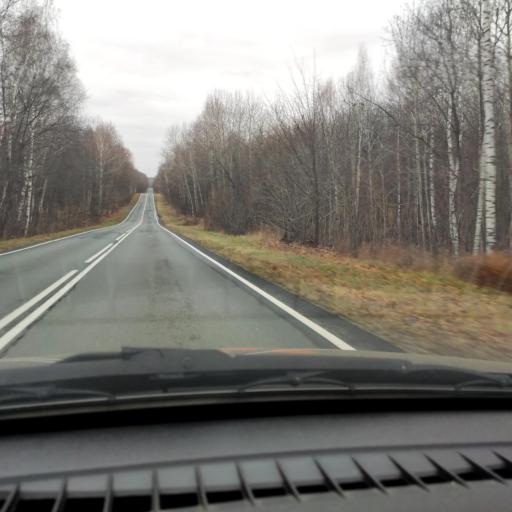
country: RU
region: Samara
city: Zhigulevsk
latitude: 53.3418
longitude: 49.5318
